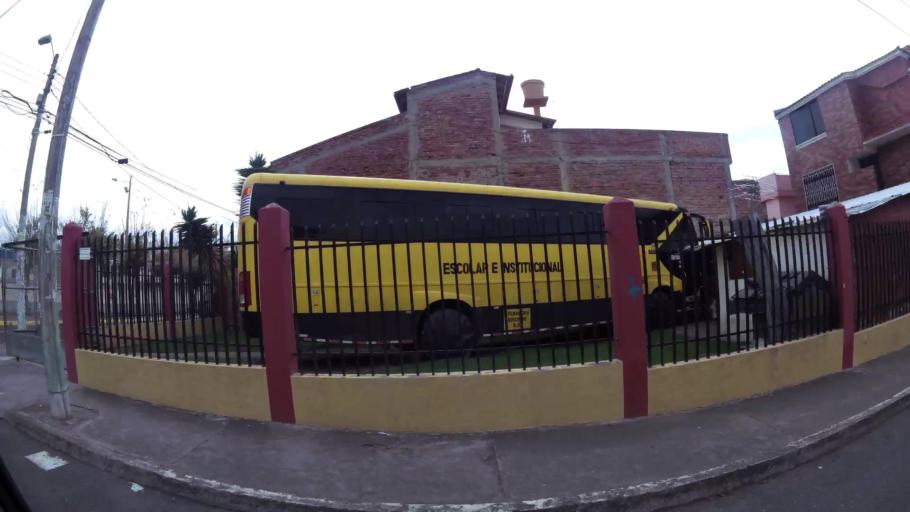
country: EC
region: Tungurahua
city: Ambato
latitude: -1.2595
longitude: -78.6270
